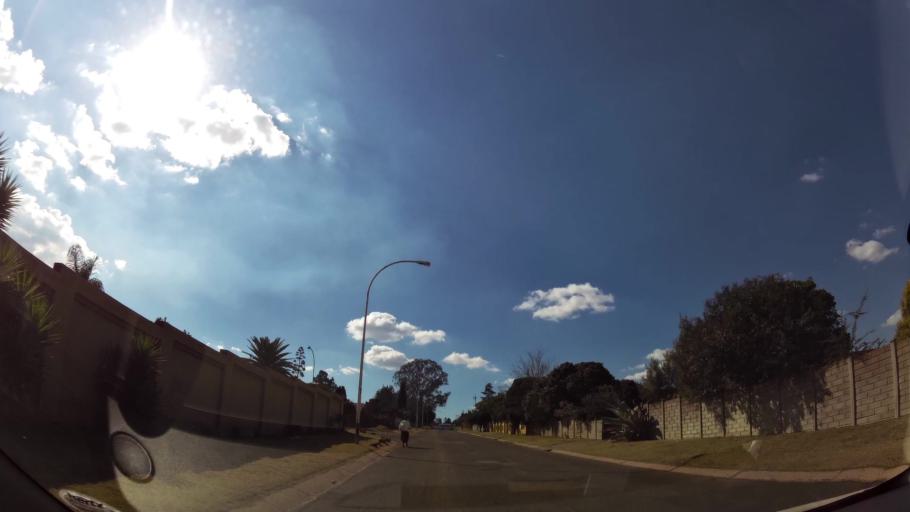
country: ZA
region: Mpumalanga
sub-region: Nkangala District Municipality
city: Witbank
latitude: -25.9289
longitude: 29.2415
